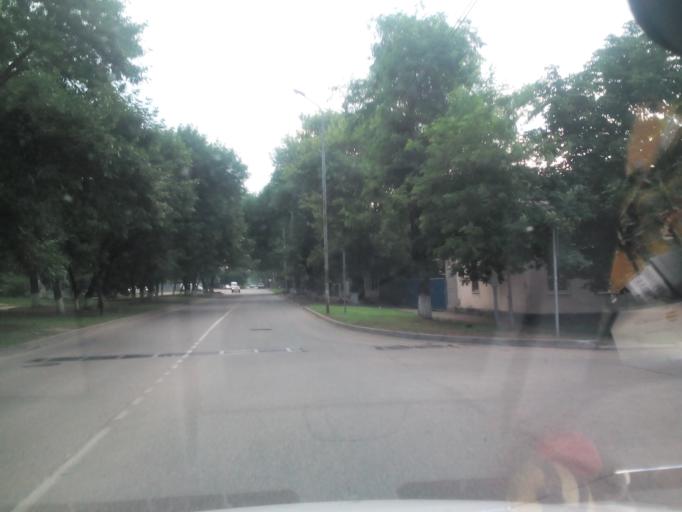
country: RU
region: Stavropol'skiy
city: Mineralnye Vody
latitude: 44.2155
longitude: 43.1293
